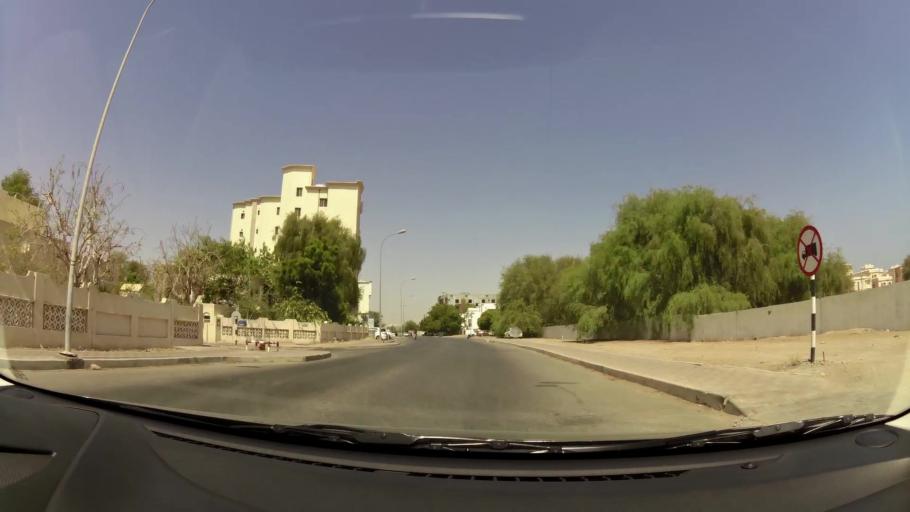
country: OM
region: Muhafazat Masqat
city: Bawshar
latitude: 23.5917
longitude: 58.3989
